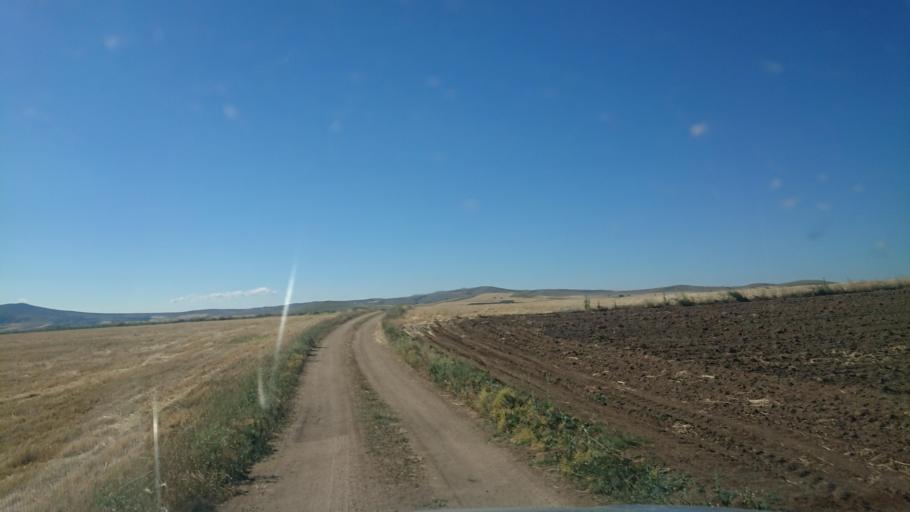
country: TR
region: Aksaray
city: Agacoren
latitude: 38.8303
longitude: 33.9522
